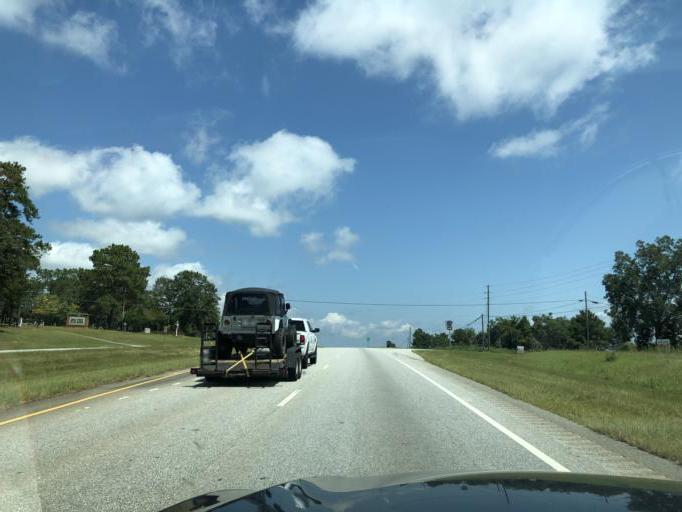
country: US
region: Alabama
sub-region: Barbour County
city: Eufaula
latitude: 31.7789
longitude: -85.1770
